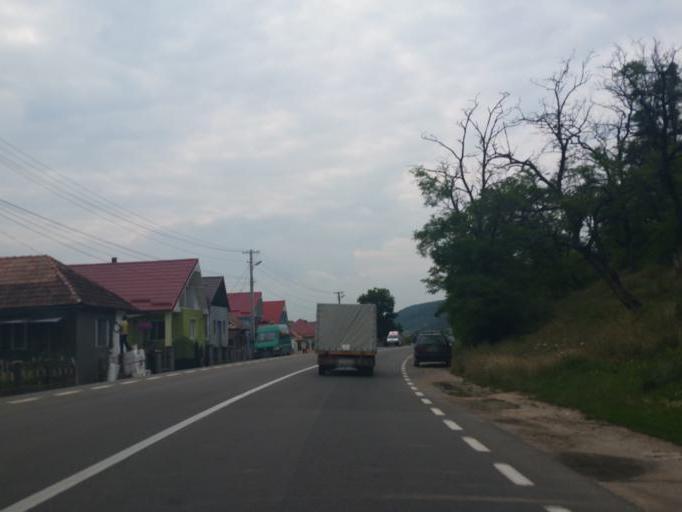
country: RO
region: Salaj
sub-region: Comuna Hida
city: Hida
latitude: 47.0477
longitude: 23.2452
